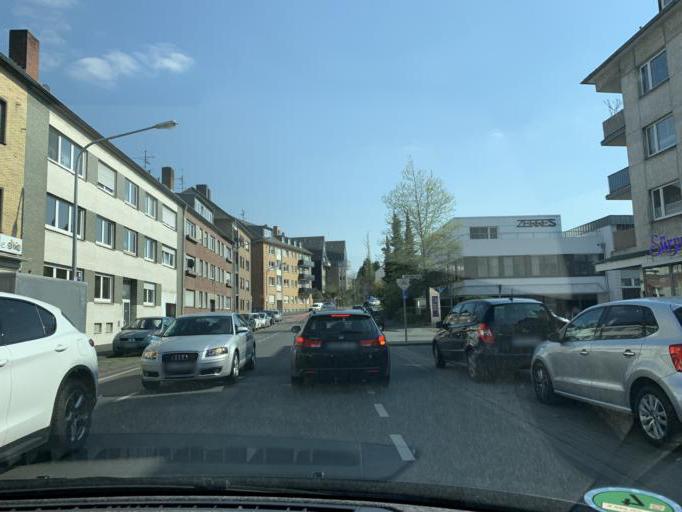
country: DE
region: North Rhine-Westphalia
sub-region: Regierungsbezirk Dusseldorf
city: Monchengladbach
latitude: 51.1504
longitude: 6.4557
